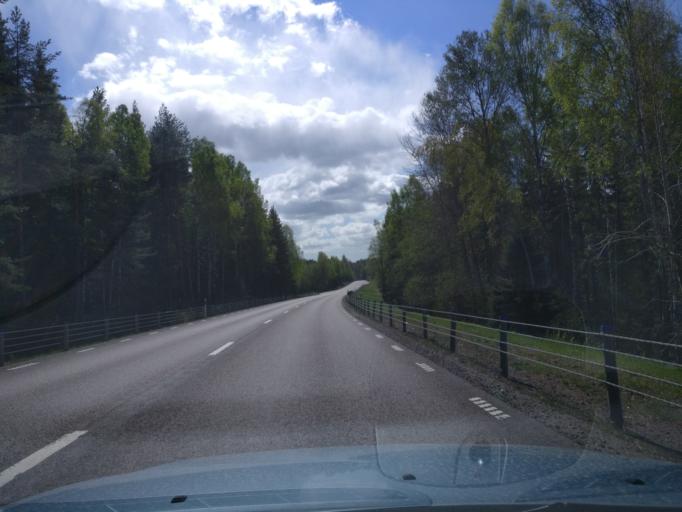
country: SE
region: Vaermland
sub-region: Karlstads Kommun
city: Molkom
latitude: 59.5747
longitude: 13.6677
